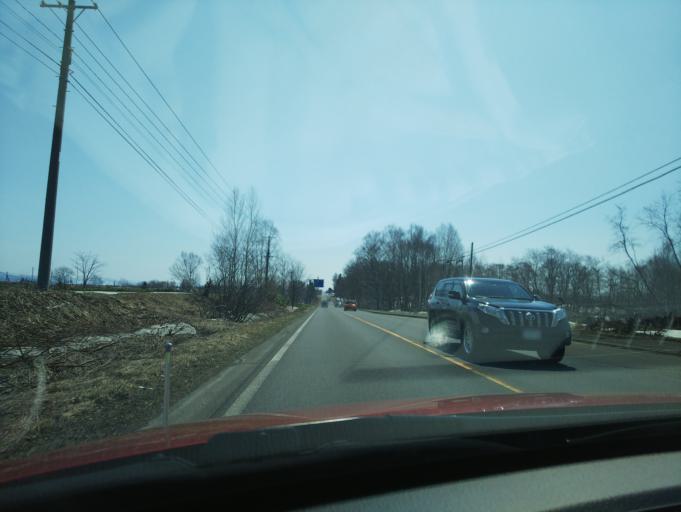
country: JP
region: Hokkaido
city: Nayoro
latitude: 44.2543
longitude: 142.3947
